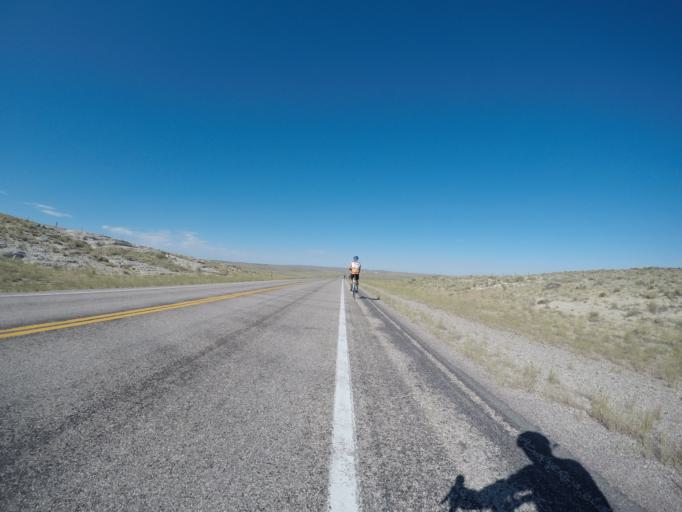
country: US
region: Wyoming
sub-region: Carbon County
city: Saratoga
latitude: 41.8694
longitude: -106.5061
